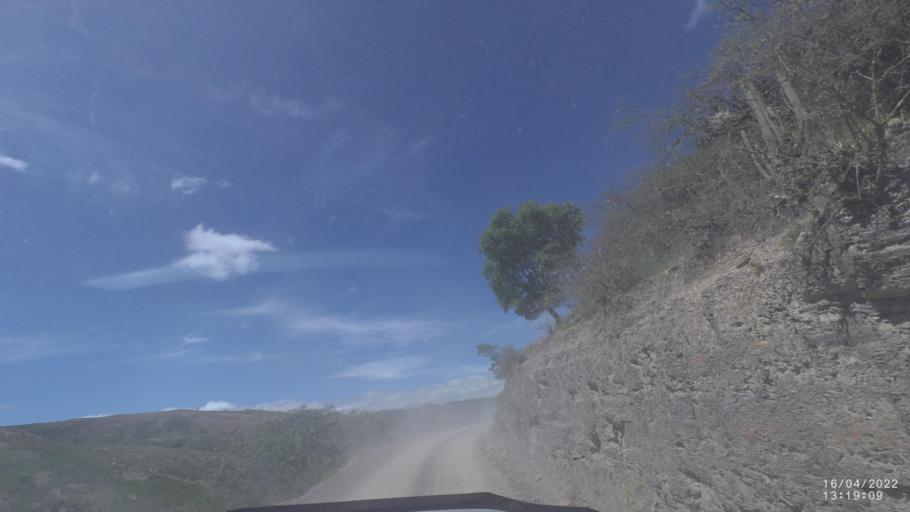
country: BO
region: Cochabamba
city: Mizque
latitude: -17.9864
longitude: -65.6168
